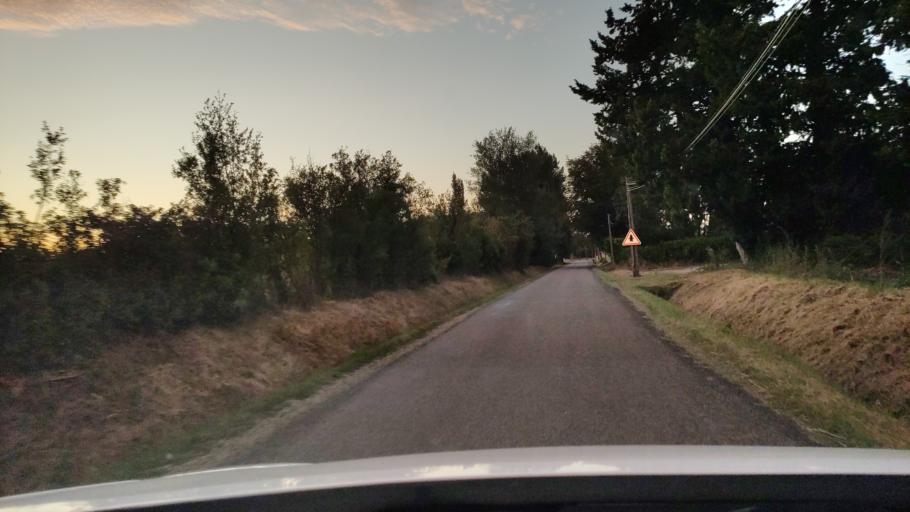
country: FR
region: Provence-Alpes-Cote d'Azur
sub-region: Departement du Vaucluse
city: Le Thor
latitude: 43.9377
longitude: 4.9805
